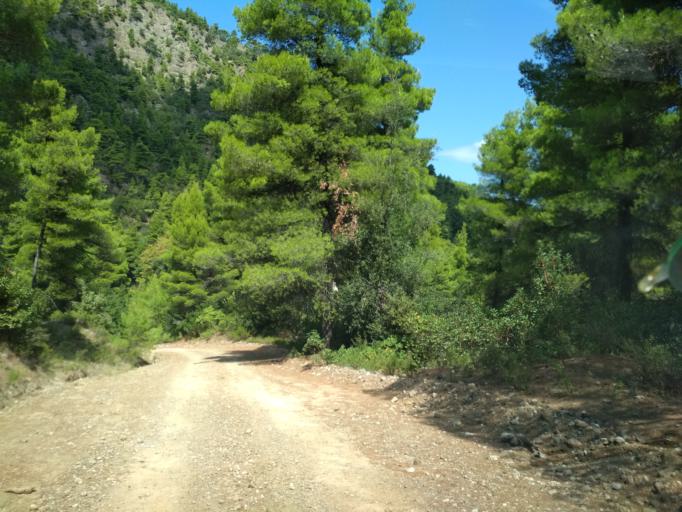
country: GR
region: Central Greece
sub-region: Nomos Evvoias
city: Roviai
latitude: 38.8427
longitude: 23.2792
